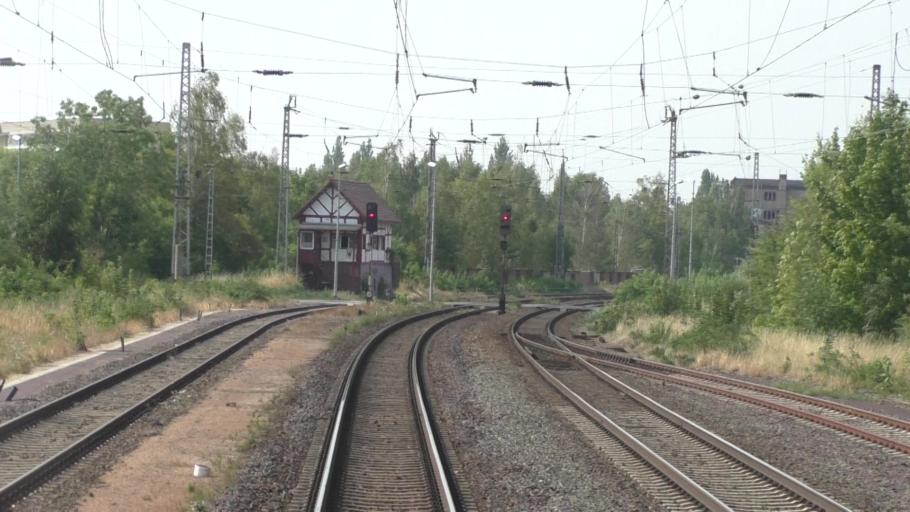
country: DE
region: Saxony-Anhalt
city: Gommern
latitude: 52.0775
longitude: 11.8319
